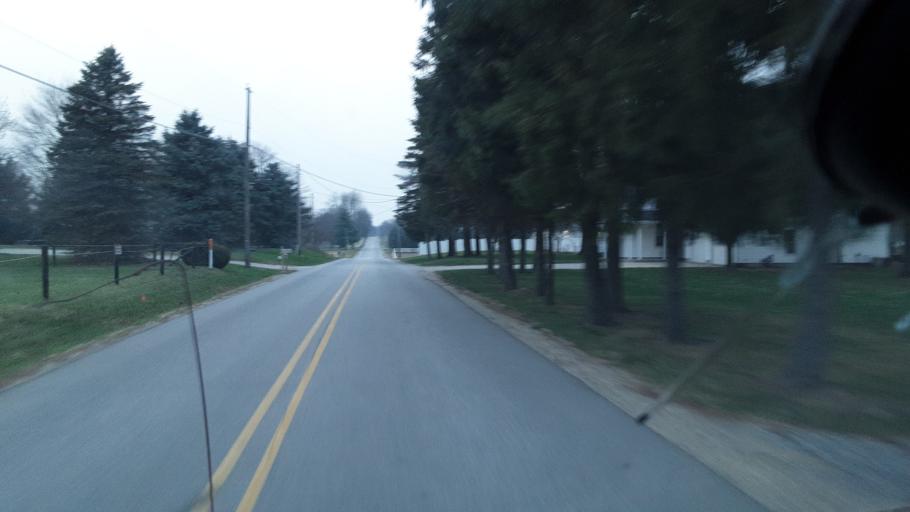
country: US
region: Indiana
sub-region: Elkhart County
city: Bristol
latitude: 41.6530
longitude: -85.7954
